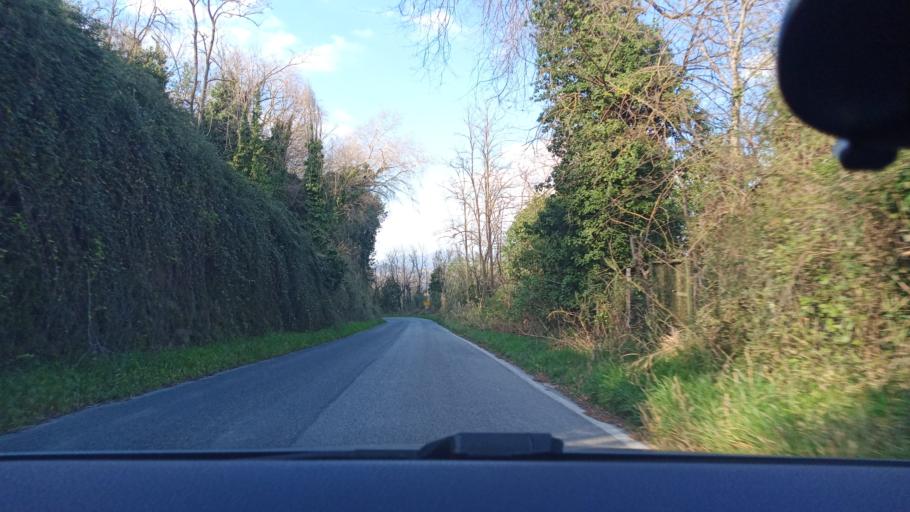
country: IT
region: Latium
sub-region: Citta metropolitana di Roma Capitale
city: Torrita Tiberina
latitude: 42.2463
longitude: 12.6184
